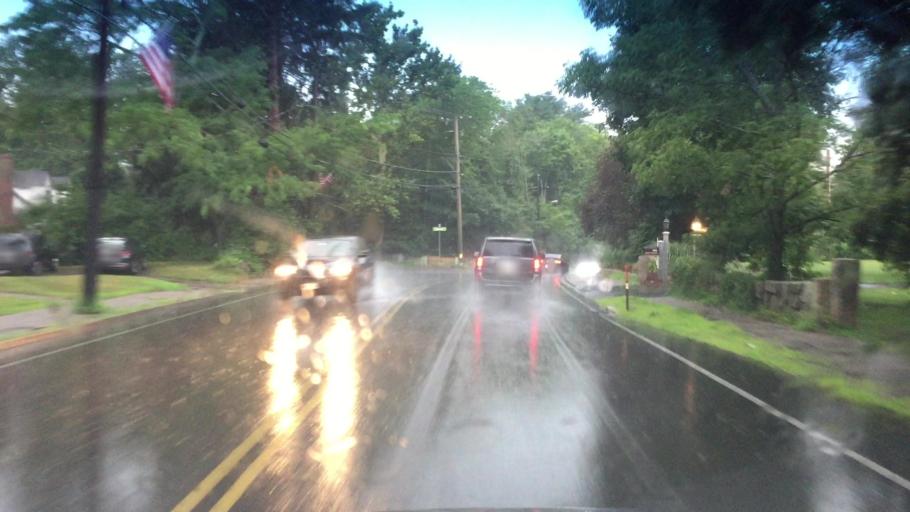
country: US
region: Massachusetts
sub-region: Norfolk County
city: Medfield
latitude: 42.1846
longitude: -71.3095
